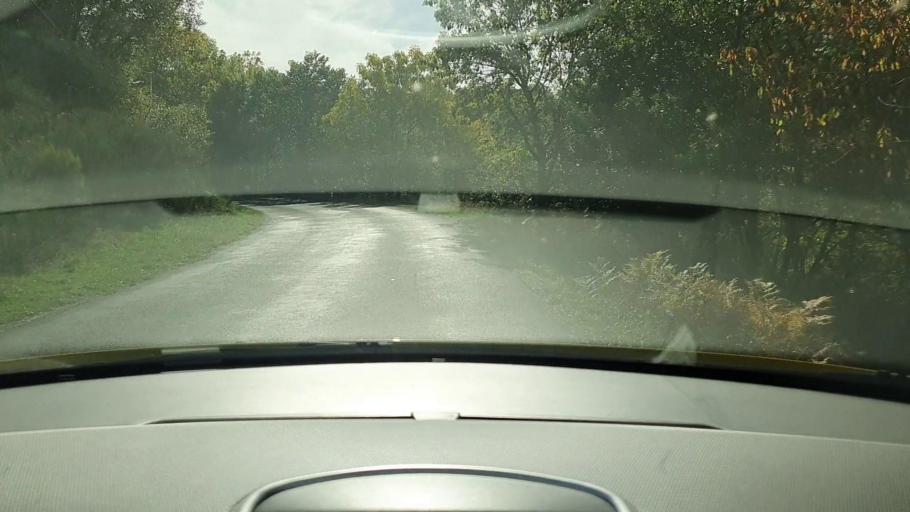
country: FR
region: Languedoc-Roussillon
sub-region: Departement de la Lozere
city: Meyrueis
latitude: 44.0690
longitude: 3.4568
